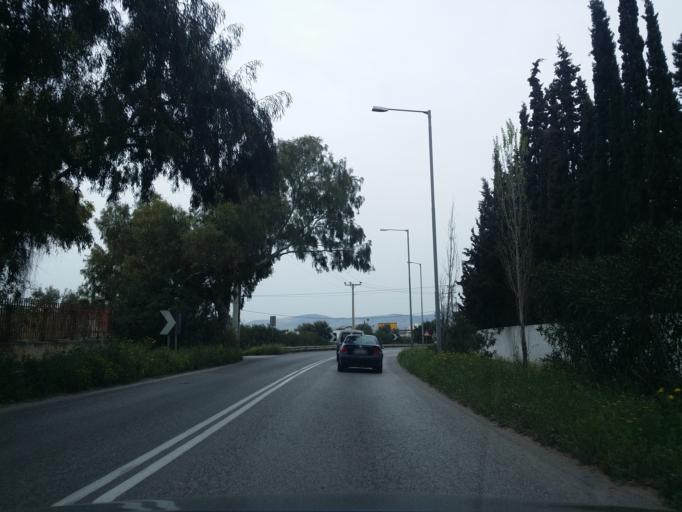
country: GR
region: Attica
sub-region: Nomarchia Dytikis Attikis
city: Mandra
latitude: 38.0772
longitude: 23.5061
